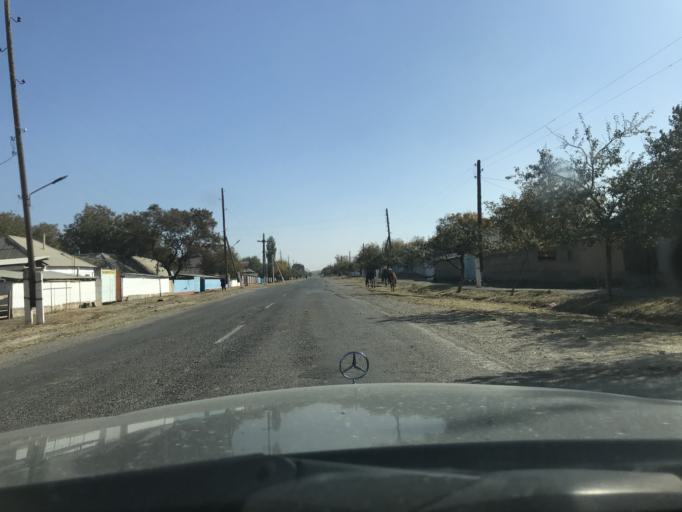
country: KZ
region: Ongtustik Qazaqstan
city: Sastobe
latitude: 42.5465
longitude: 69.9252
